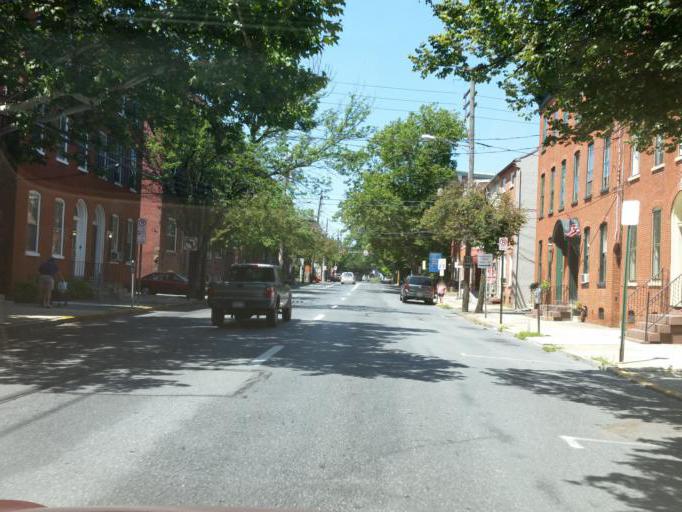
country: US
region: Pennsylvania
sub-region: Lancaster County
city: Lancaster
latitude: 40.0431
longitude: -76.3030
